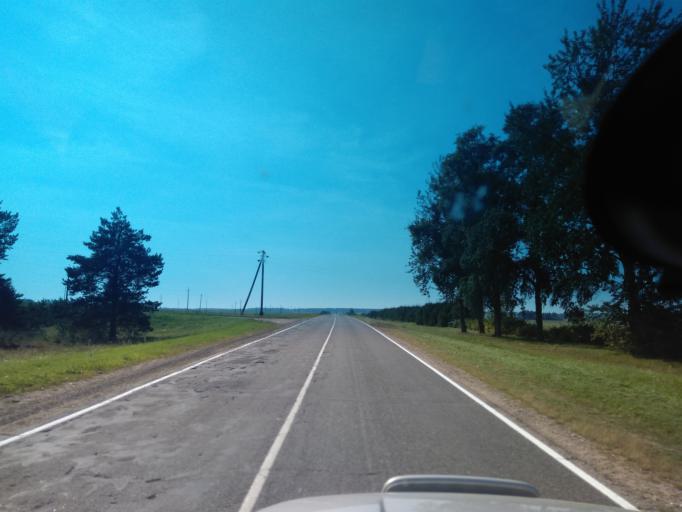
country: BY
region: Minsk
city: Uzda
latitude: 53.3814
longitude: 27.2399
